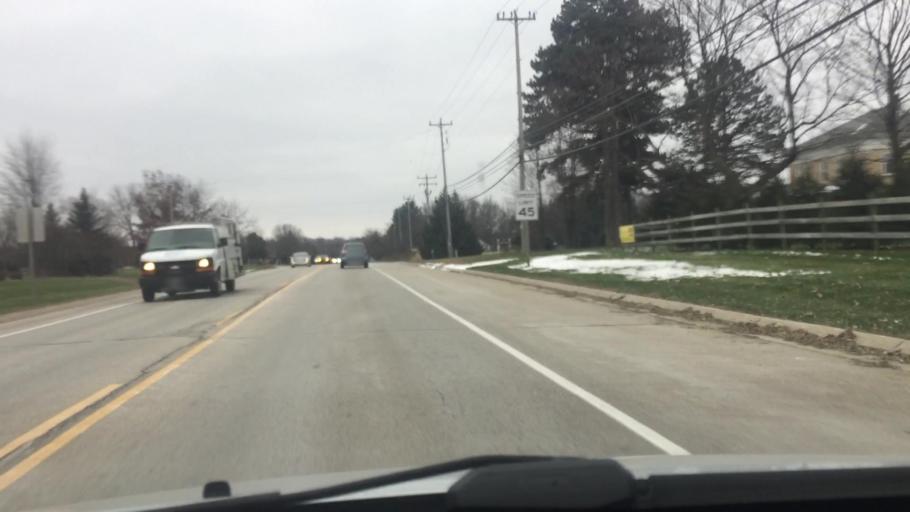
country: US
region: Wisconsin
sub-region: Waukesha County
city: Hartland
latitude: 43.0858
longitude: -88.3632
